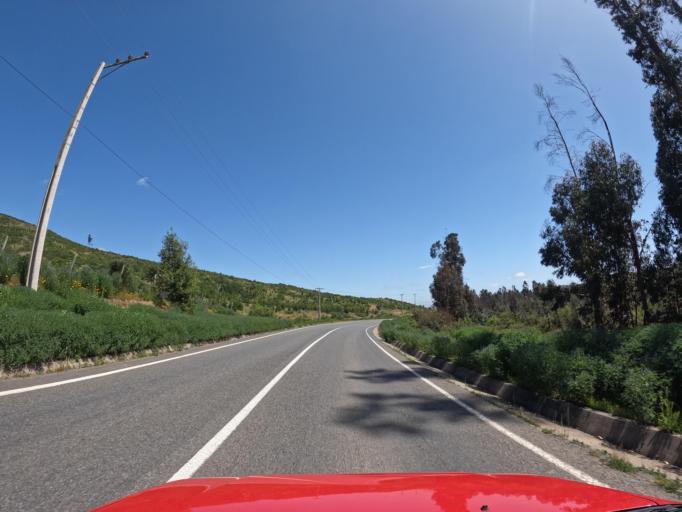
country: CL
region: O'Higgins
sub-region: Provincia de Colchagua
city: Santa Cruz
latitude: -34.6691
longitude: -71.8220
